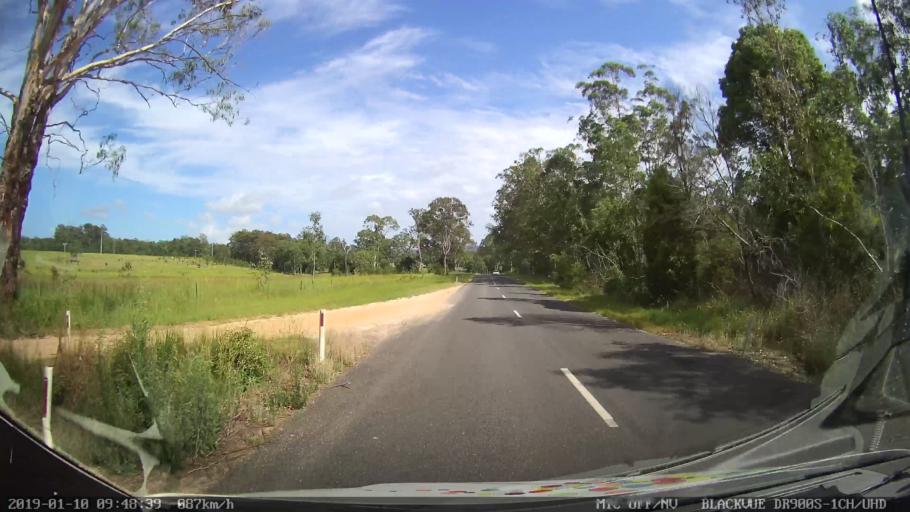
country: AU
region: New South Wales
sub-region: Coffs Harbour
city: Nana Glen
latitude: -30.0702
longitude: 152.9856
